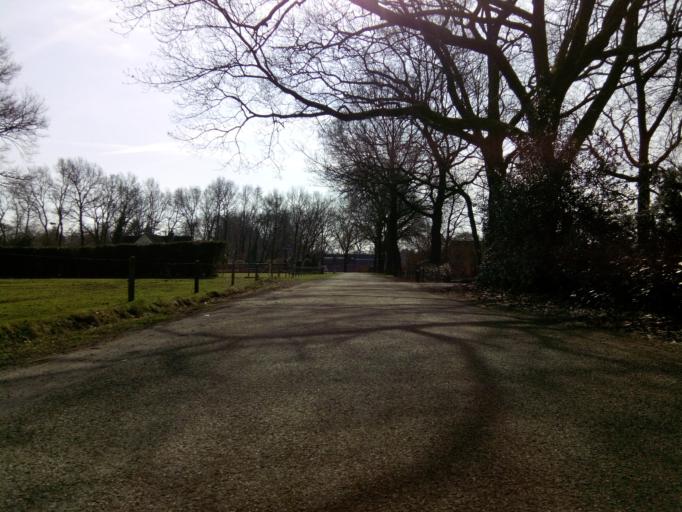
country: NL
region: Gelderland
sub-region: Gemeente Barneveld
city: Voorthuizen
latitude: 52.2148
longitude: 5.6247
